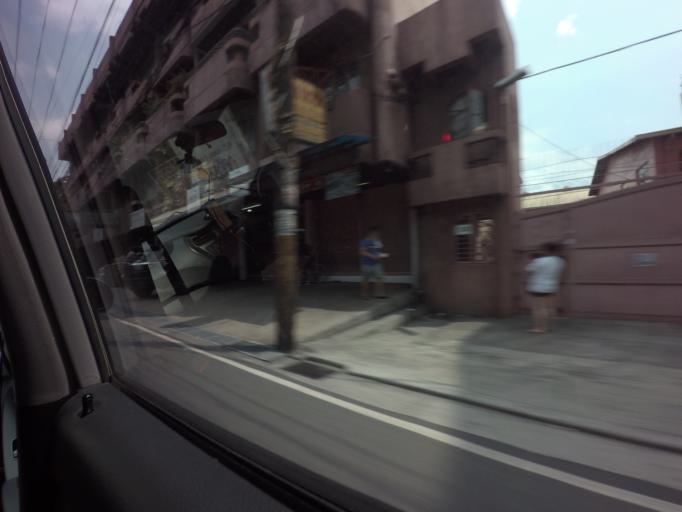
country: PH
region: Metro Manila
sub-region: San Juan
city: San Juan
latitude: 14.5981
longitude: 121.0151
